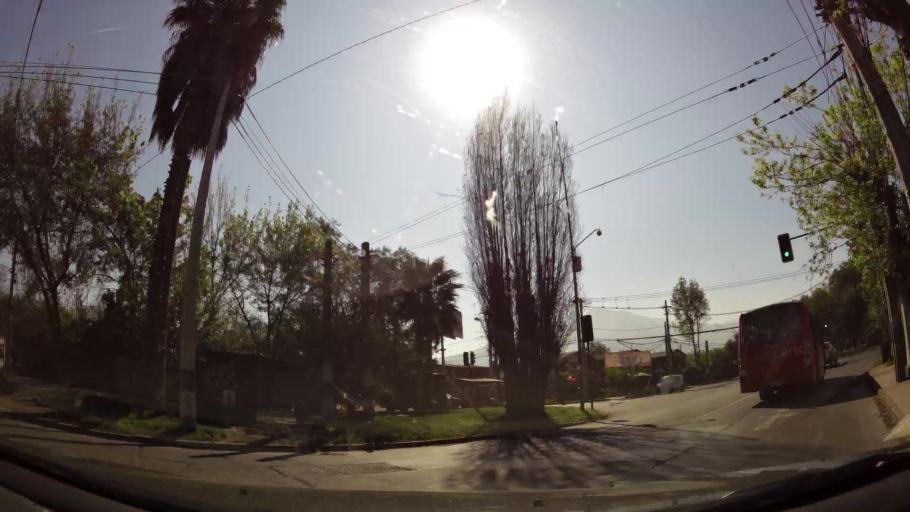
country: CL
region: Santiago Metropolitan
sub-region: Provincia de Chacabuco
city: Chicureo Abajo
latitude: -33.3594
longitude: -70.6827
